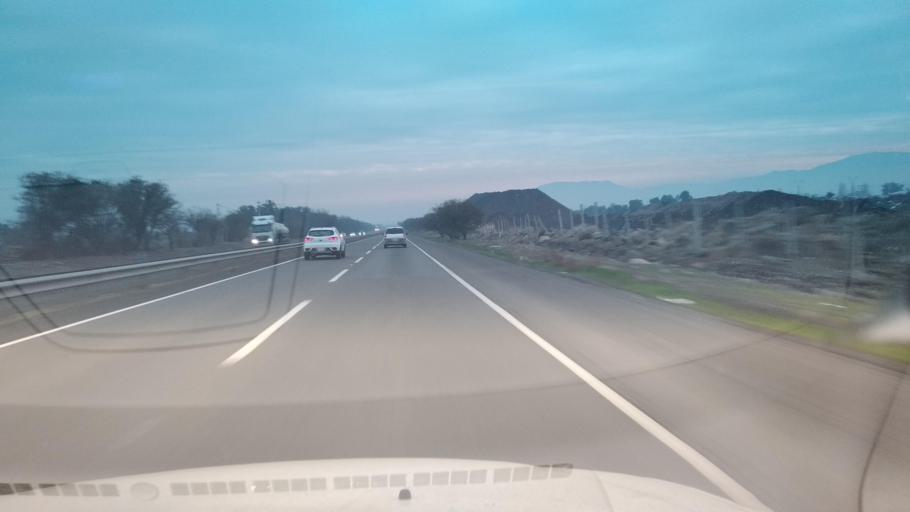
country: CL
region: Santiago Metropolitan
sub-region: Provincia de Chacabuco
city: Chicureo Abajo
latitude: -33.1987
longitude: -70.6602
